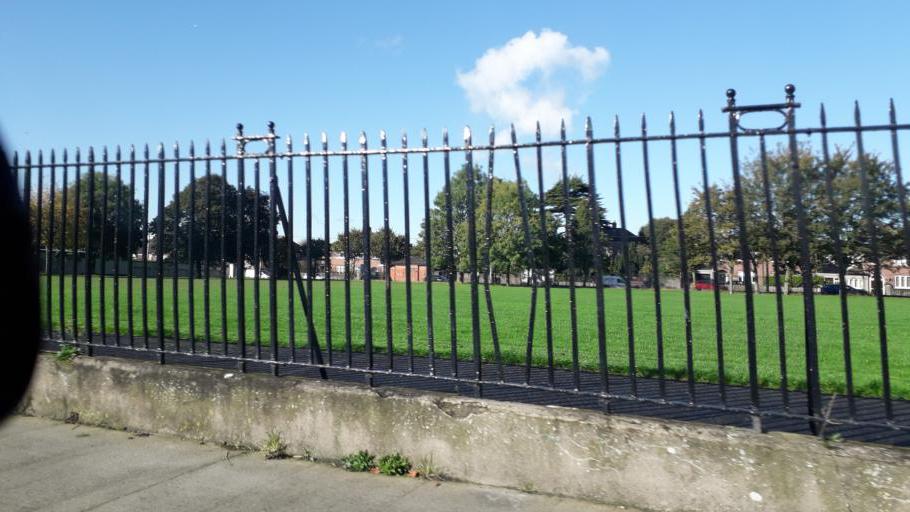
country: IE
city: Donnycarney
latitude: 53.3766
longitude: -6.2150
